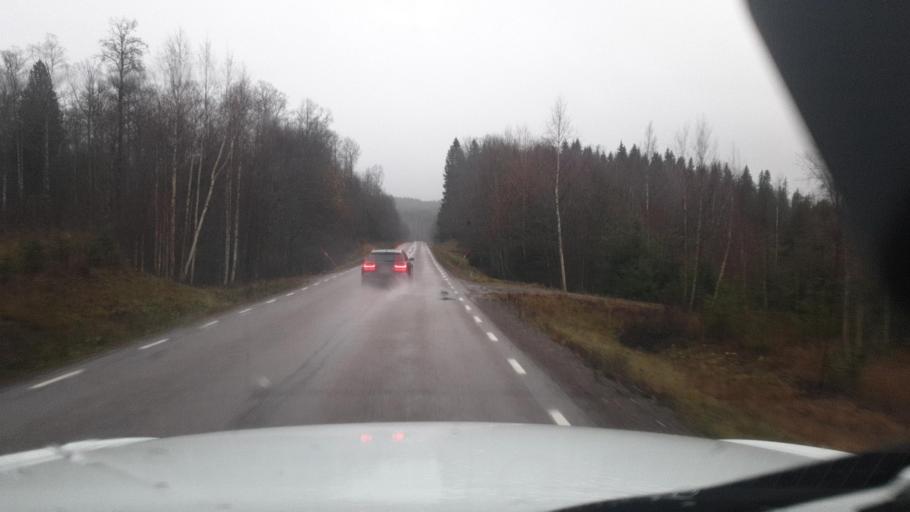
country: SE
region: Vaermland
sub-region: Arvika Kommun
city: Arvika
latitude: 59.9545
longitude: 12.7249
